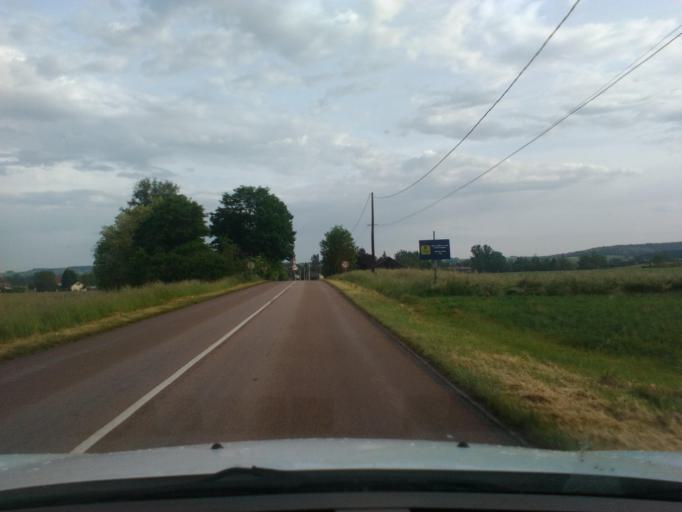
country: FR
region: Lorraine
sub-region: Departement de Meurthe-et-Moselle
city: Gerbeviller
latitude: 48.4318
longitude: 6.5790
